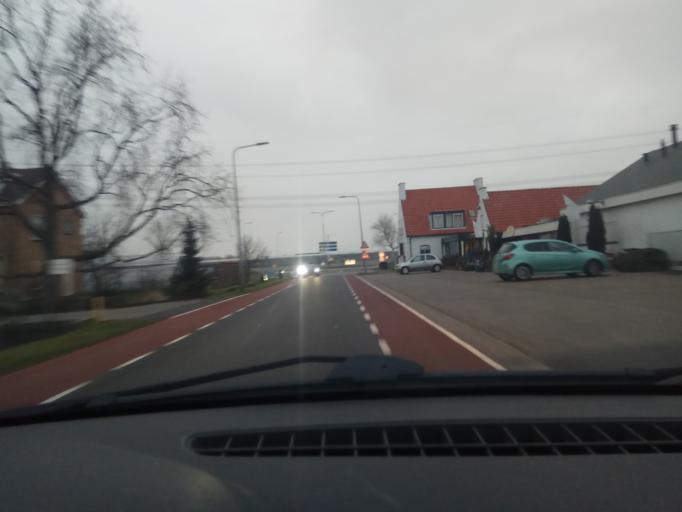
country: NL
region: South Holland
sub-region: Gemeente Westland
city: Maasdijk
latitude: 51.9675
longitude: 4.1986
